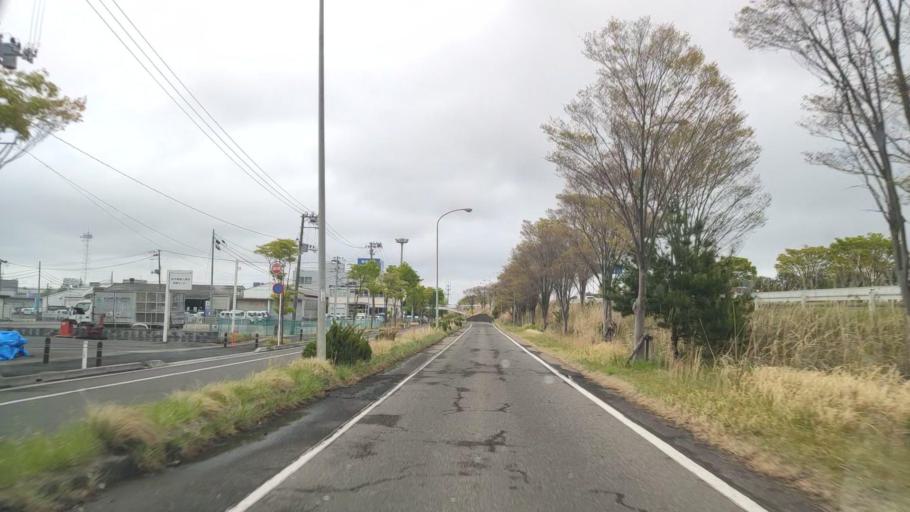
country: JP
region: Miyagi
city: Sendai-shi
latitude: 38.2657
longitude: 140.9380
